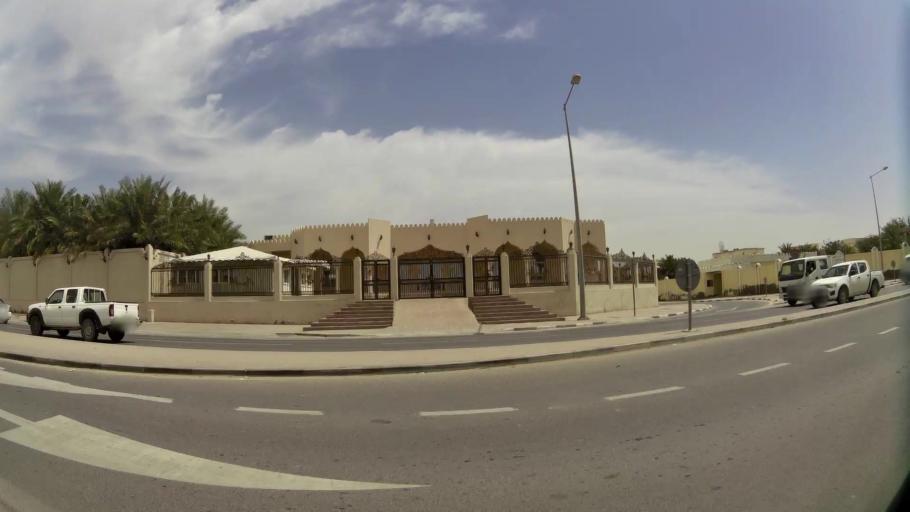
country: QA
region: Baladiyat ar Rayyan
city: Ar Rayyan
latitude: 25.2802
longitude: 51.4202
